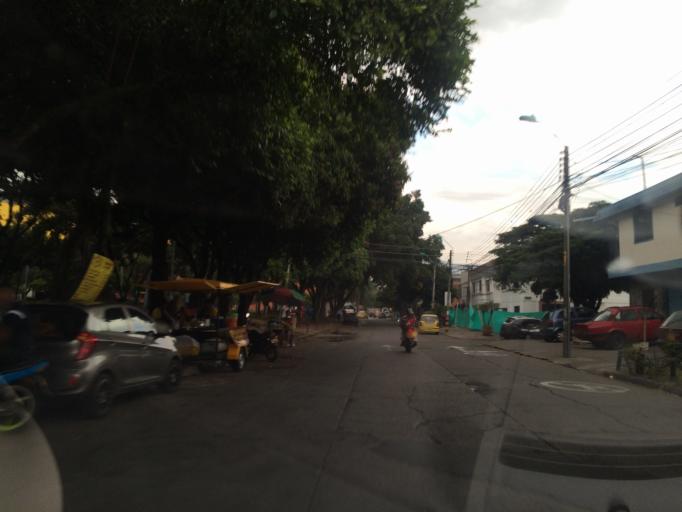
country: CO
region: Valle del Cauca
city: Cali
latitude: 3.4243
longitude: -76.5439
